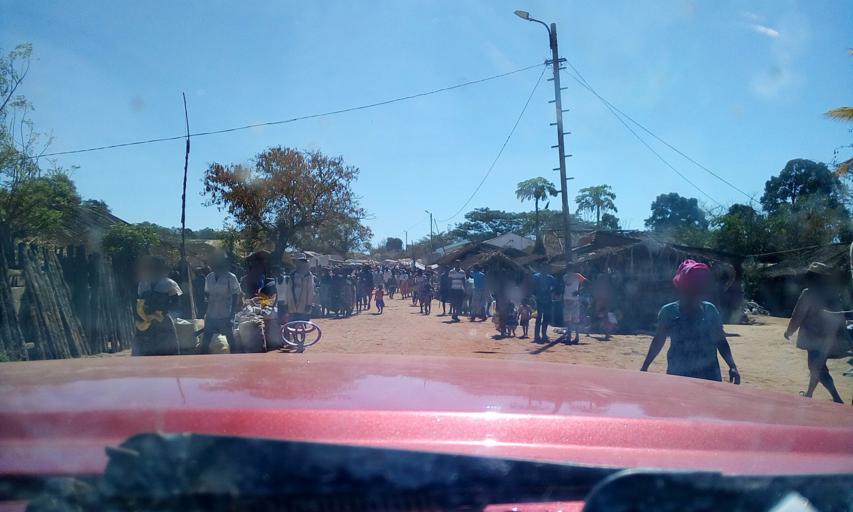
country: MG
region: Boeny
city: Mahajanga
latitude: -15.9575
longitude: 45.9398
